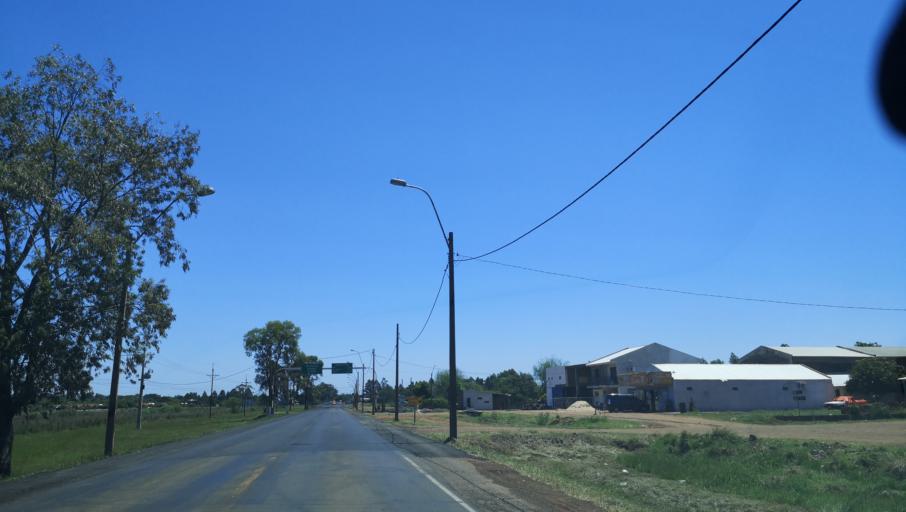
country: PY
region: Itapua
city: Carmen del Parana
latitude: -27.2203
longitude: -56.1330
